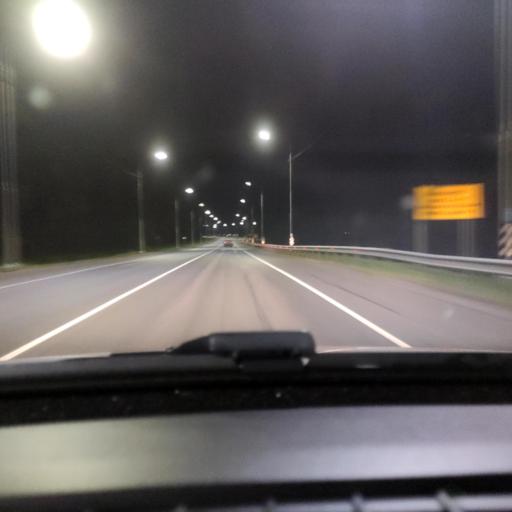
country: RU
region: Voronezj
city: Kashirskoye
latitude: 51.5010
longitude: 39.5750
